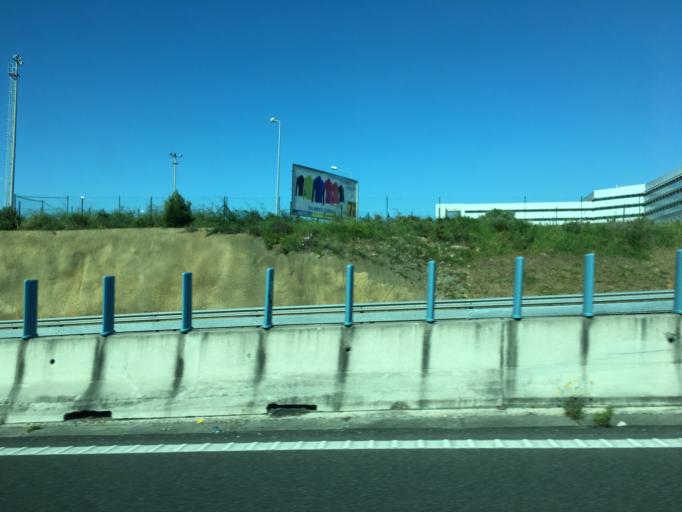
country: PT
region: Lisbon
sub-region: Cascais
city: Alcabideche
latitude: 38.7294
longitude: -9.4154
